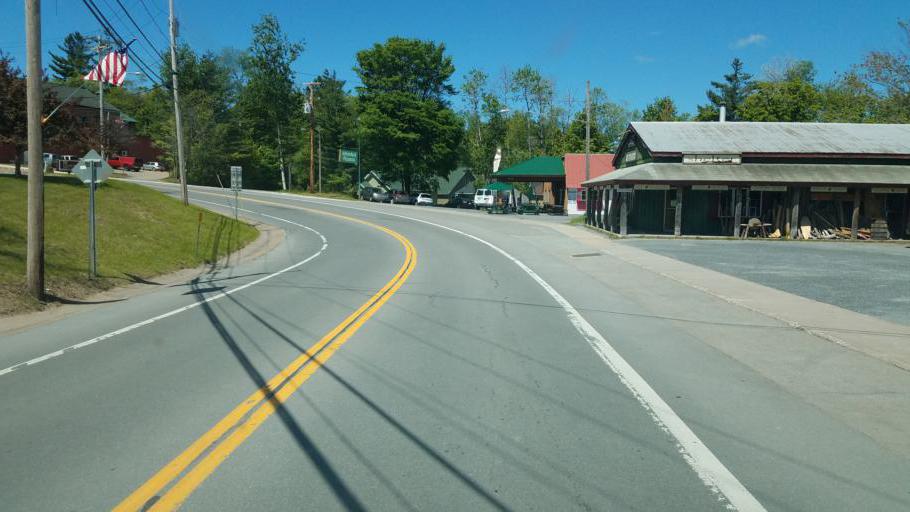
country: US
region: New York
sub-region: Oneida County
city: Boonville
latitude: 43.7113
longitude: -74.9712
